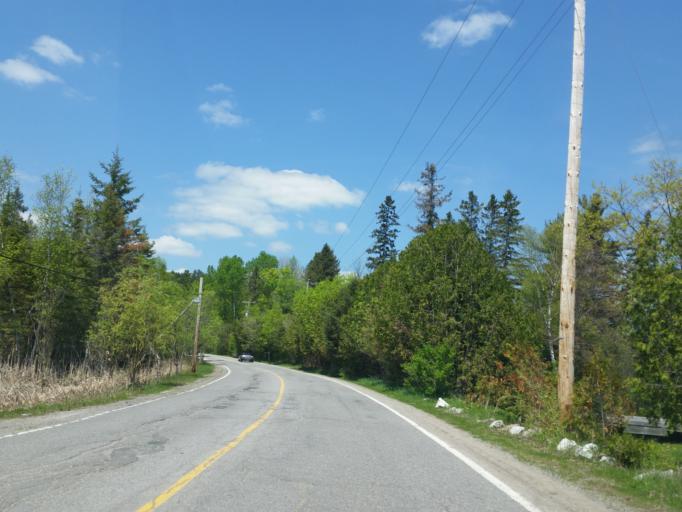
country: CA
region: Quebec
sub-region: Outaouais
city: Wakefield
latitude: 45.6079
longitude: -75.8946
